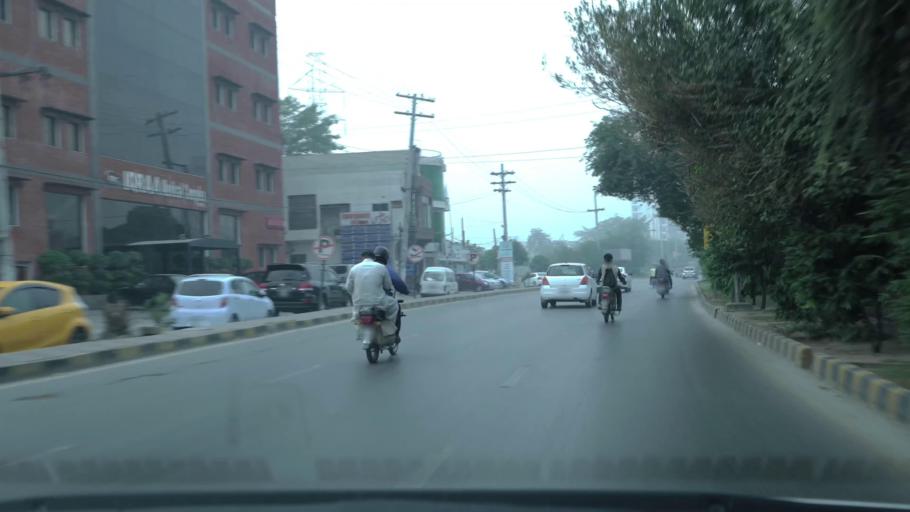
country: PK
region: Punjab
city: Lahore
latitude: 31.4714
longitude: 74.3029
